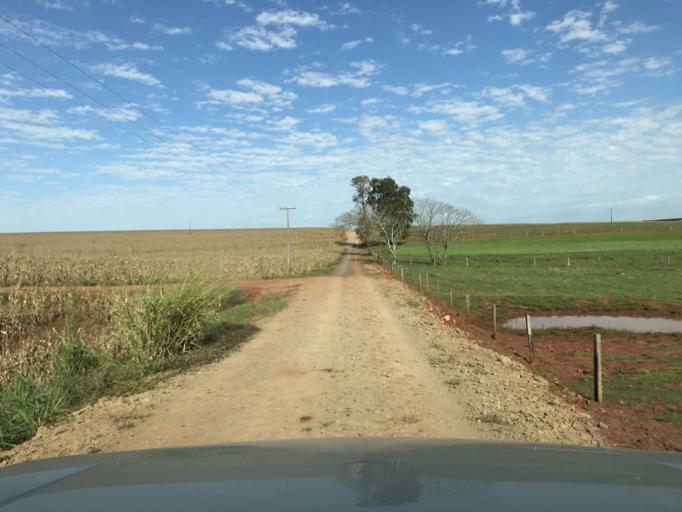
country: BR
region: Parana
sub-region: Palotina
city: Palotina
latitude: -24.1661
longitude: -53.7525
